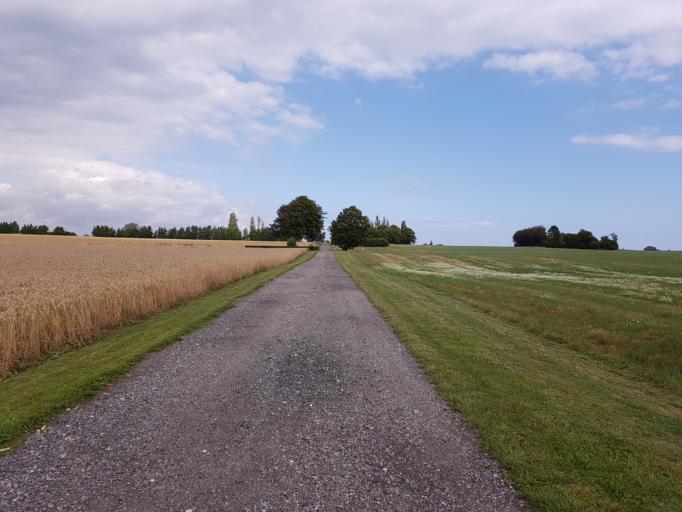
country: DK
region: Zealand
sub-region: Guldborgsund Kommune
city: Nykobing Falster
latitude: 54.5808
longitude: 11.9424
